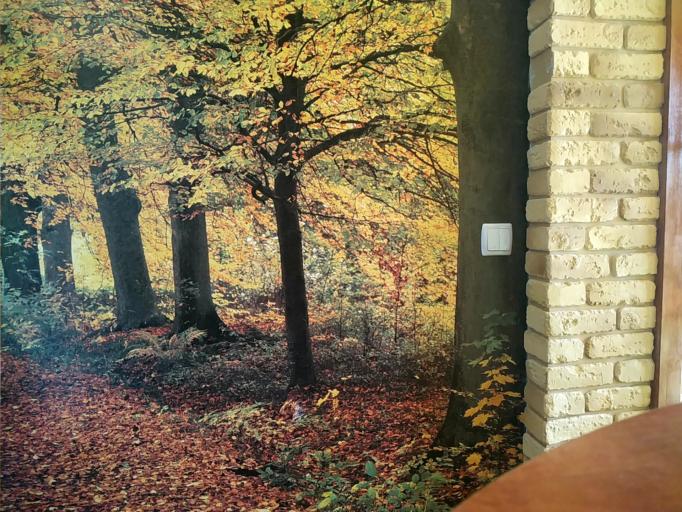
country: RU
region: Vologda
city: Molochnoye
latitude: 58.9565
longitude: 39.6442
